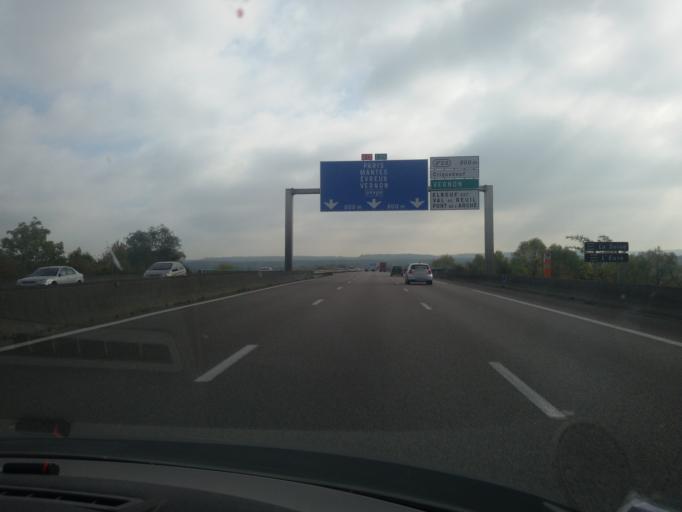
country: FR
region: Haute-Normandie
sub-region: Departement de l'Eure
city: Criquebeuf-sur-Seine
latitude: 49.3112
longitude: 1.1115
